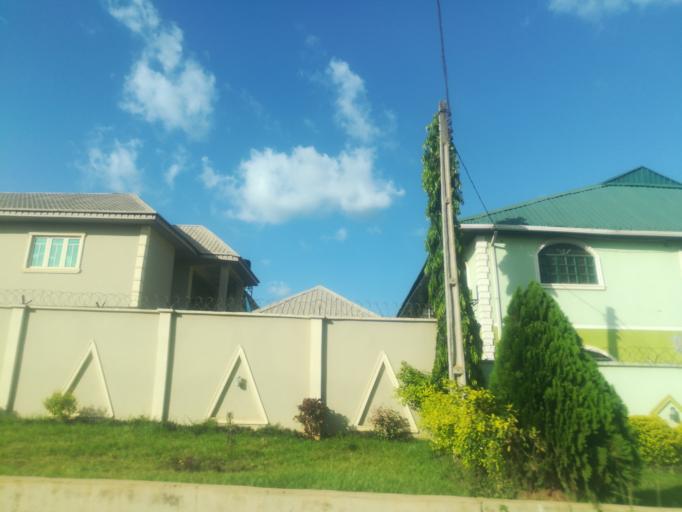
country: NG
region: Oyo
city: Ibadan
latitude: 7.4354
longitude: 3.9729
